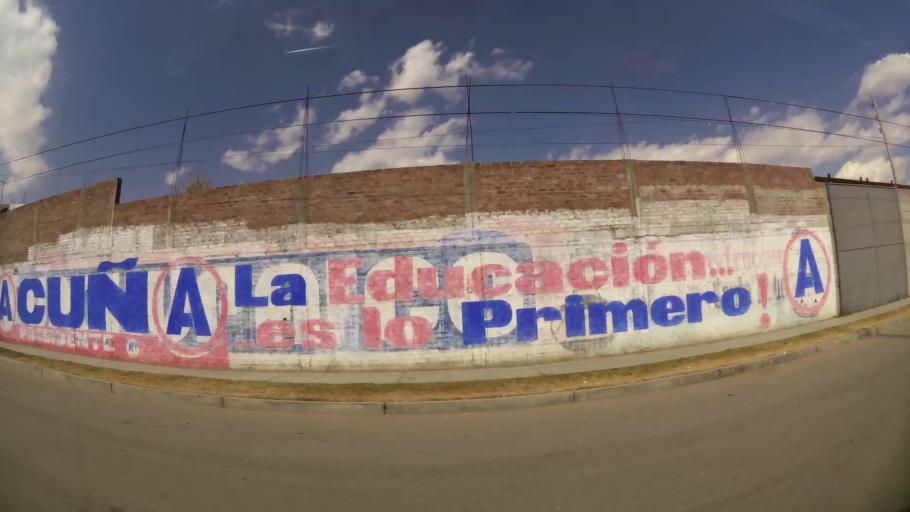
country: PE
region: Junin
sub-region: Provincia de Huancayo
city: El Tambo
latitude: -12.0768
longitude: -75.2148
